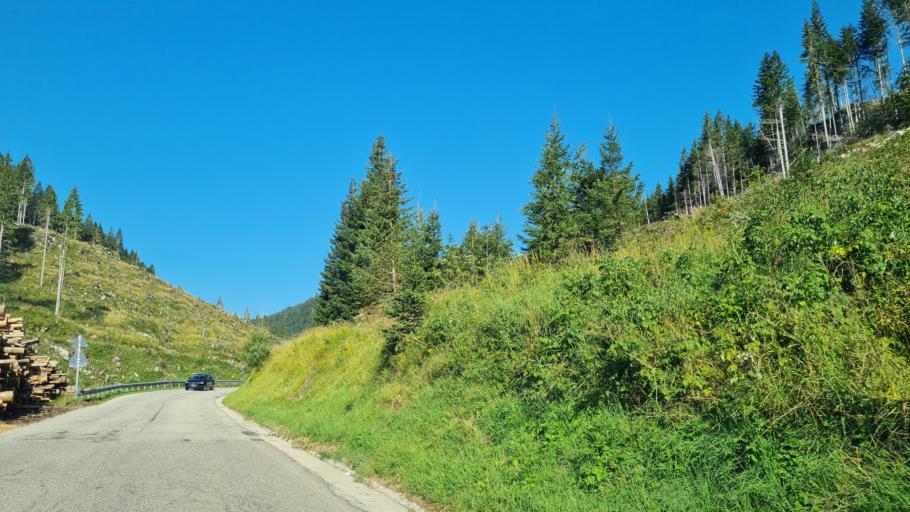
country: IT
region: Veneto
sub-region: Provincia di Vicenza
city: San Pietro Valdastico
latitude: 45.9503
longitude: 11.3933
